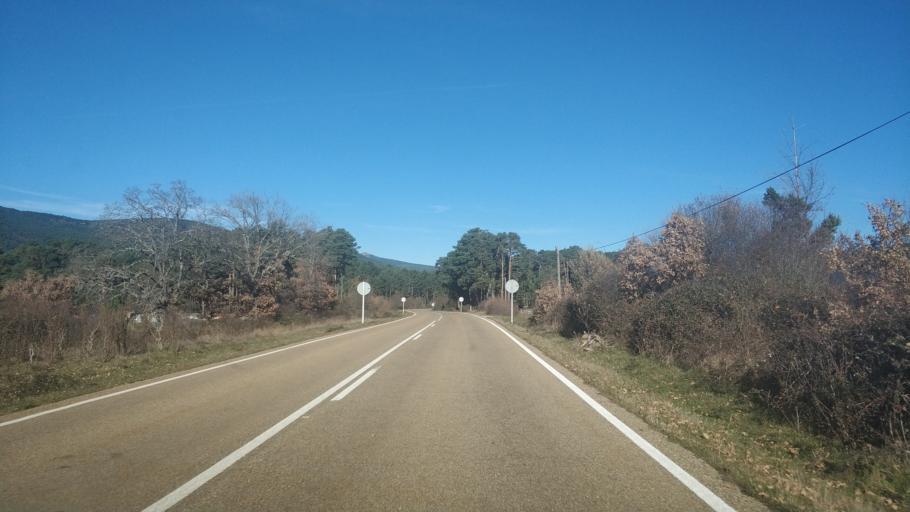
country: ES
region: Castille and Leon
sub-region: Provincia de Soria
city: Vinuesa
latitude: 41.9220
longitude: -2.7610
